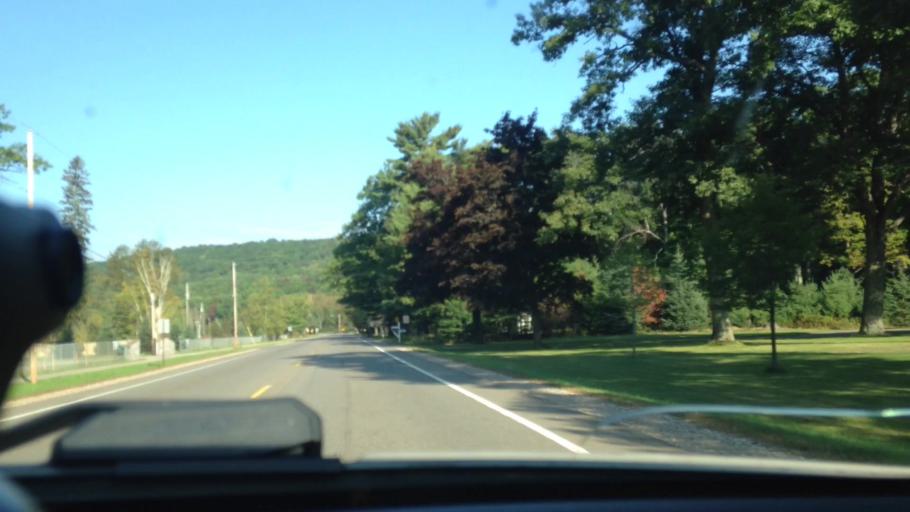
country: US
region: Michigan
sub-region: Dickinson County
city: Quinnesec
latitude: 45.8406
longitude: -88.0146
